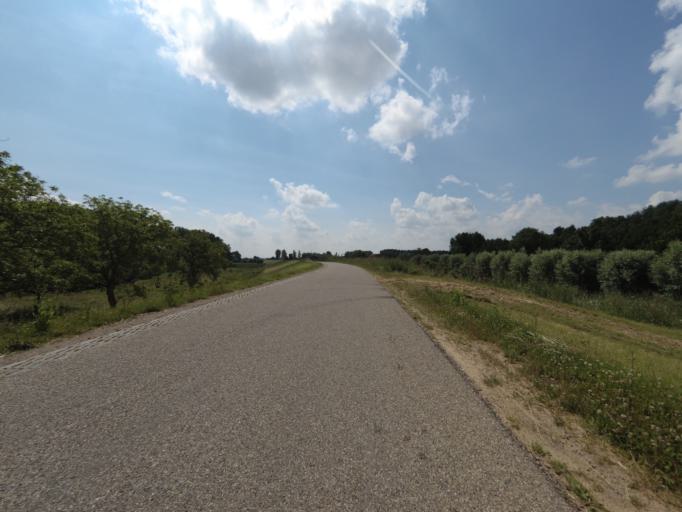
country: NL
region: Gelderland
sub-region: Gemeente Culemborg
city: Culemborg
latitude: 51.9686
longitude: 5.2529
